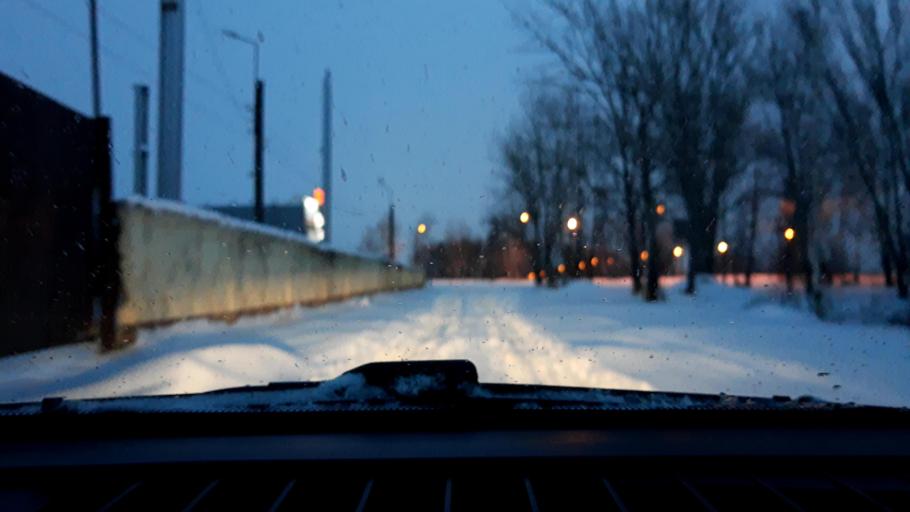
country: RU
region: Nizjnij Novgorod
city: Neklyudovo
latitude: 56.3458
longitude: 43.8874
